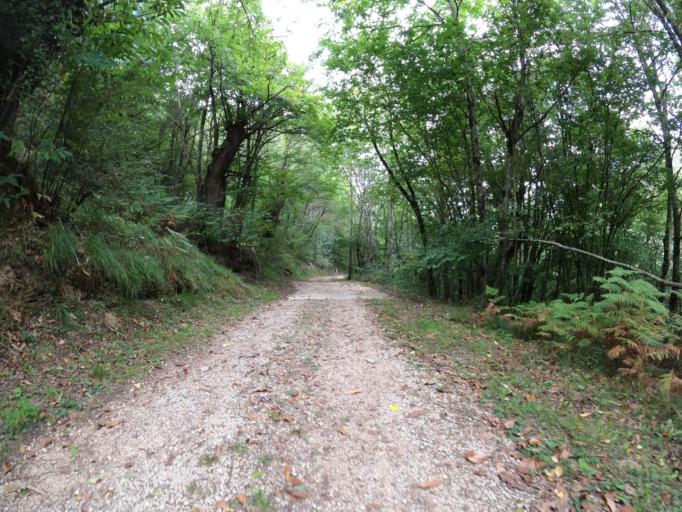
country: ES
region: Navarre
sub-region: Provincia de Navarra
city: Irurtzun
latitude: 42.9649
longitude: -1.8380
